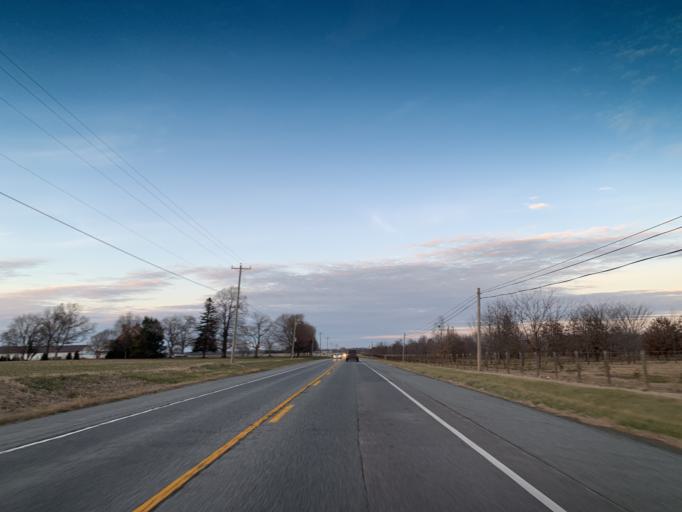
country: US
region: Delaware
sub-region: New Castle County
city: Middletown
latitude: 39.4211
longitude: -75.8607
